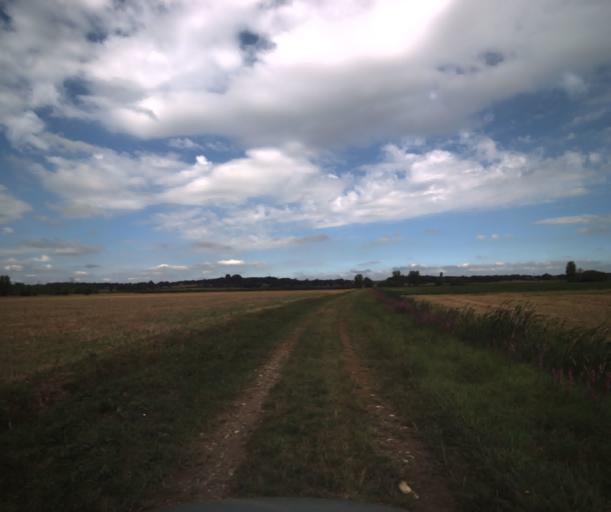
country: FR
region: Midi-Pyrenees
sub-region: Departement de la Haute-Garonne
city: Lherm
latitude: 43.3972
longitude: 1.2292
